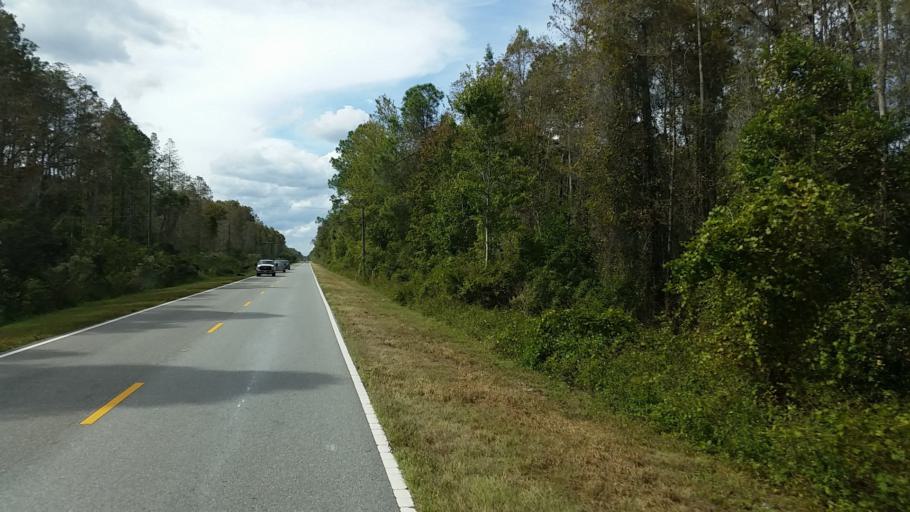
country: US
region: Florida
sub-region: Lake County
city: Four Corners
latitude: 28.3755
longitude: -81.7599
